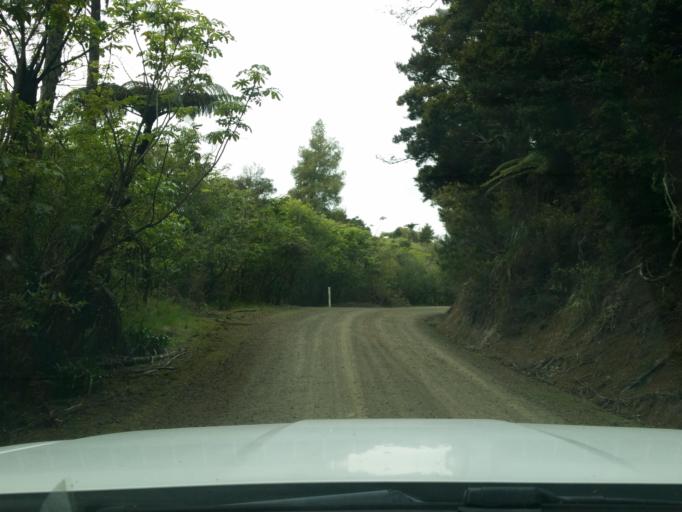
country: NZ
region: Northland
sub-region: Kaipara District
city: Dargaville
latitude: -35.7128
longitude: 173.6274
